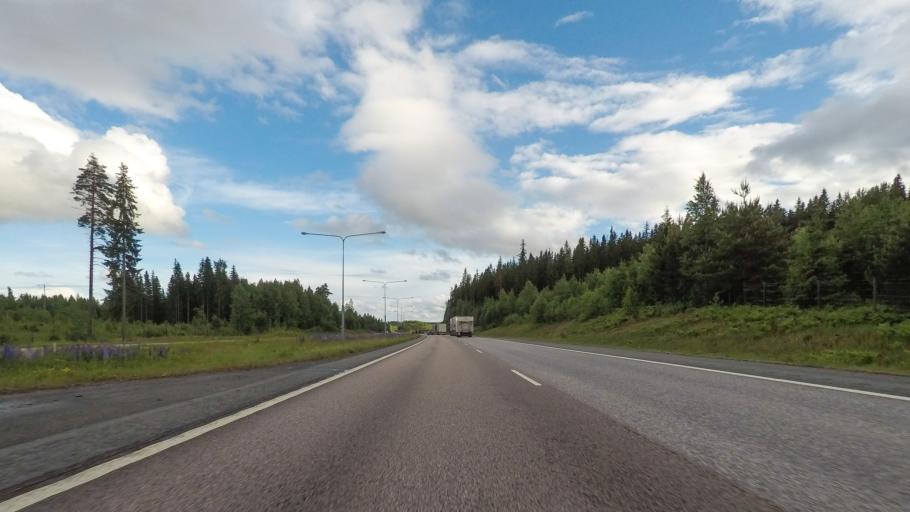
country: FI
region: Paijanne Tavastia
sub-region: Lahti
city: Heinola
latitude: 61.2703
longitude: 26.0620
